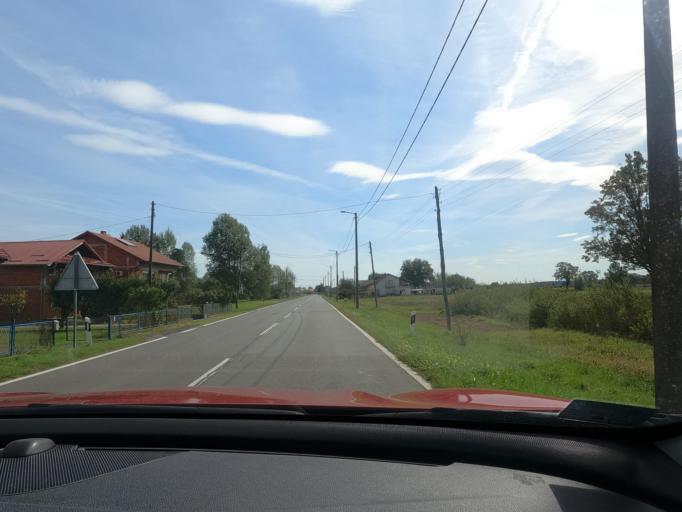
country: HR
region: Sisacko-Moslavacka
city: Budasevo
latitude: 45.4889
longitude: 16.4579
